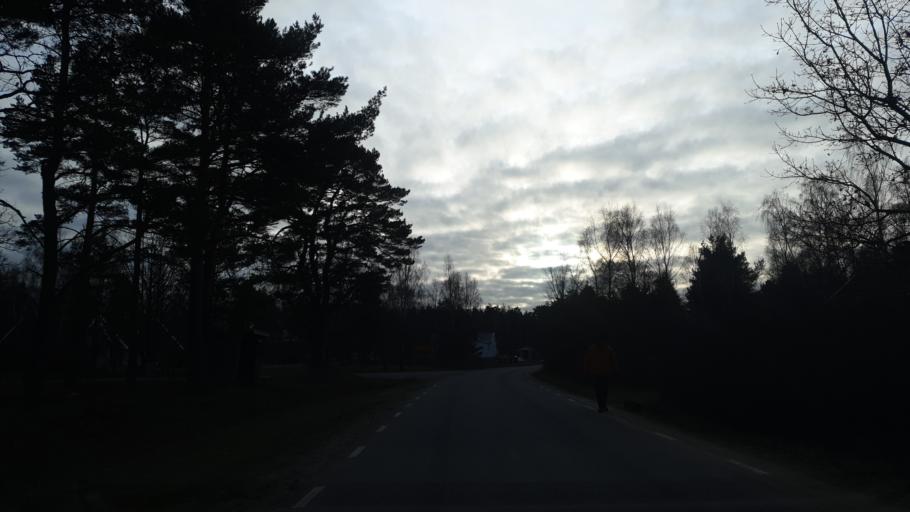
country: SE
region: Kalmar
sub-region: Torsas Kommun
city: Torsas
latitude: 56.3116
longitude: 16.0337
